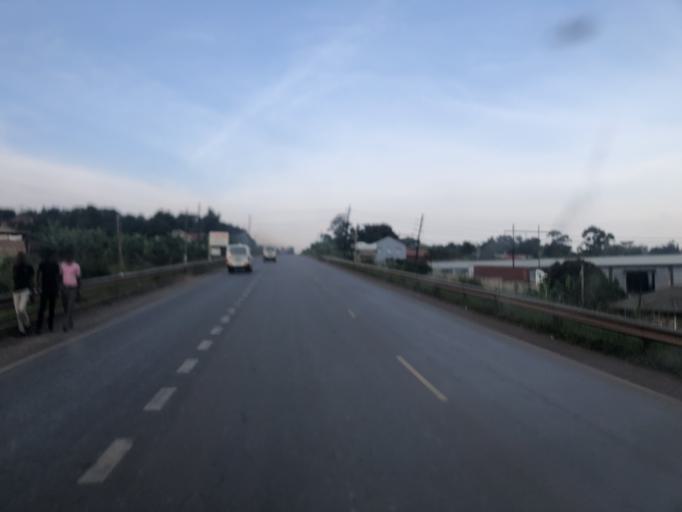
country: UG
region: Central Region
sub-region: Mpigi District
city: Mpigi
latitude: 0.2435
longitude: 32.3730
